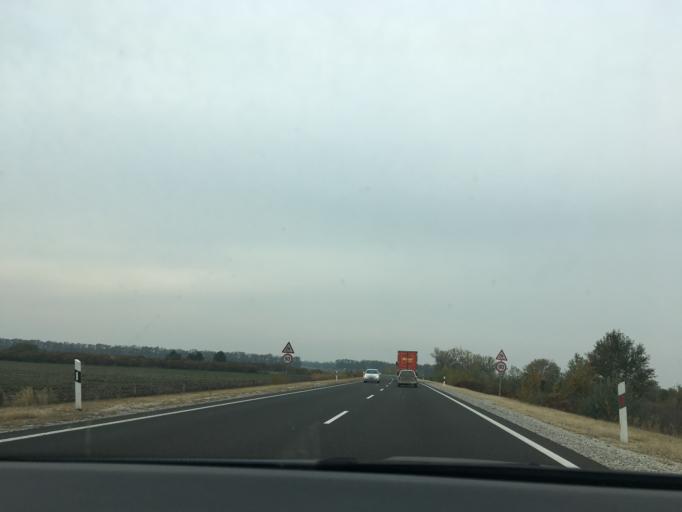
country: HU
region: Jasz-Nagykun-Szolnok
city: Kisujszallas
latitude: 47.2465
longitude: 20.7327
